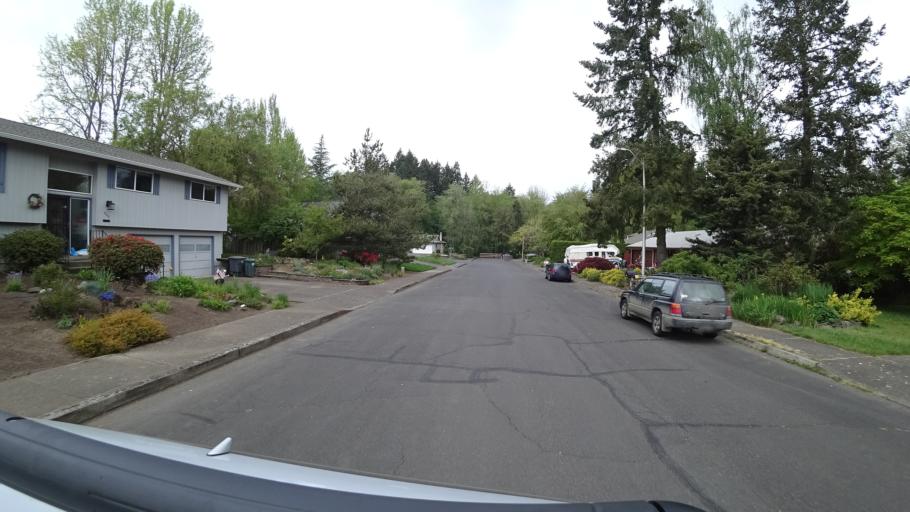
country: US
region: Oregon
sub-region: Washington County
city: Hillsboro
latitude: 45.5328
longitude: -122.9819
